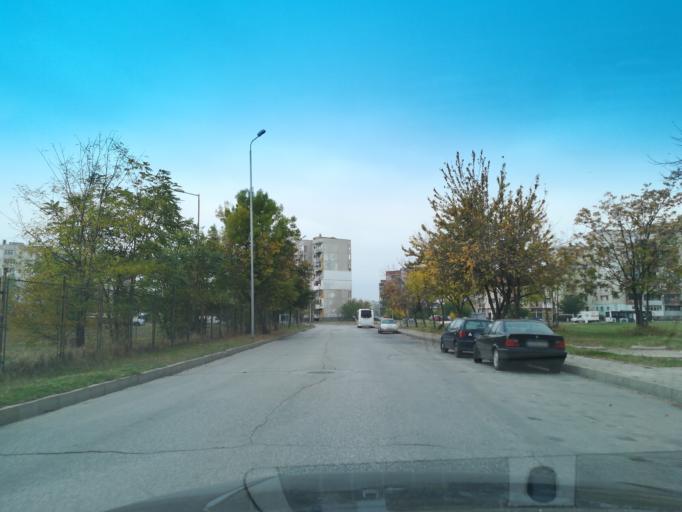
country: BG
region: Plovdiv
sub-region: Obshtina Plovdiv
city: Plovdiv
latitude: 42.1434
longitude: 24.7995
